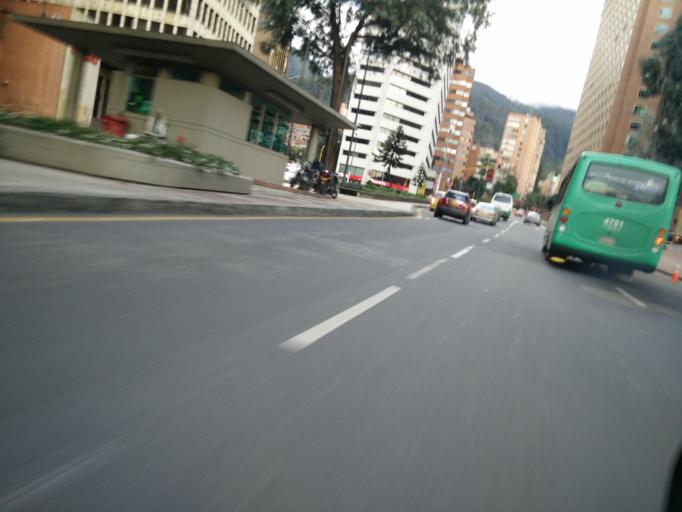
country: CO
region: Bogota D.C.
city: Barrio San Luis
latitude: 4.6553
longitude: -74.0561
